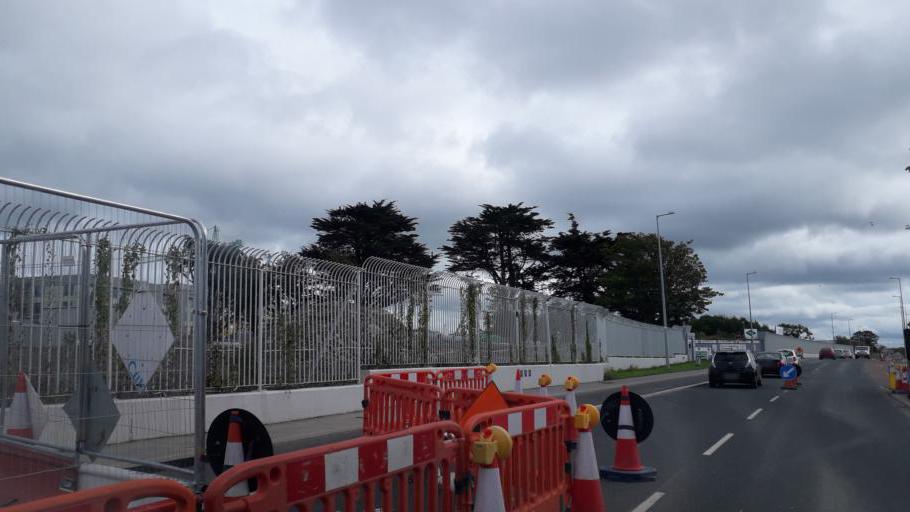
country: IE
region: Leinster
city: Cabinteely
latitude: 53.2751
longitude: -6.1549
